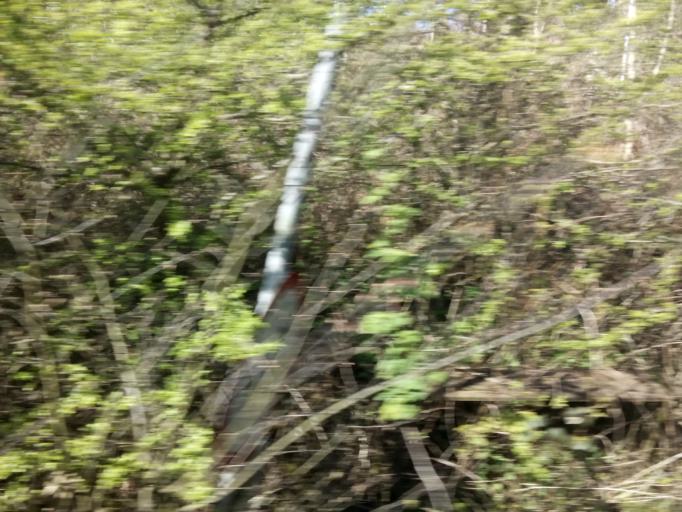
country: GB
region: Scotland
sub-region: Fife
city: Inverkeithing
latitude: 56.0365
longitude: -3.3956
